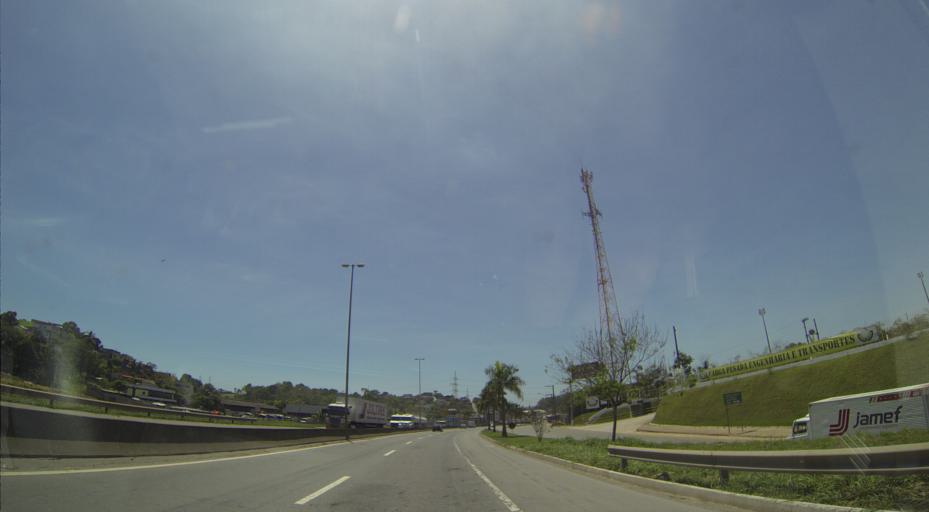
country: BR
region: Espirito Santo
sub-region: Viana
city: Viana
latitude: -20.3575
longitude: -40.4297
